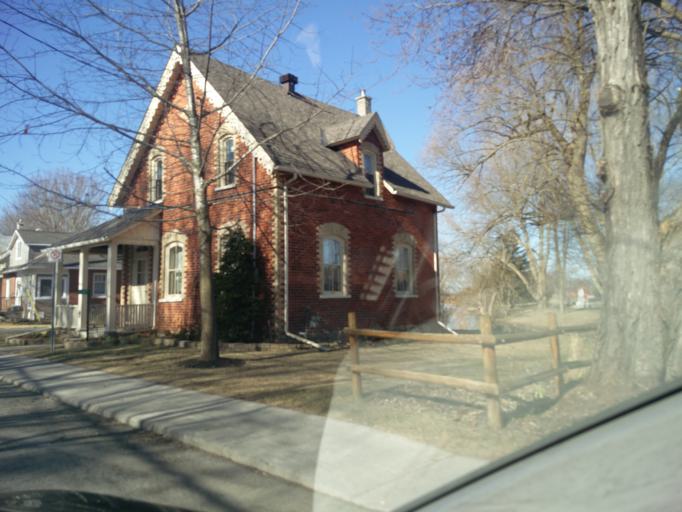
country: CA
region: Ontario
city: Bells Corners
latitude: 45.1296
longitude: -75.7158
